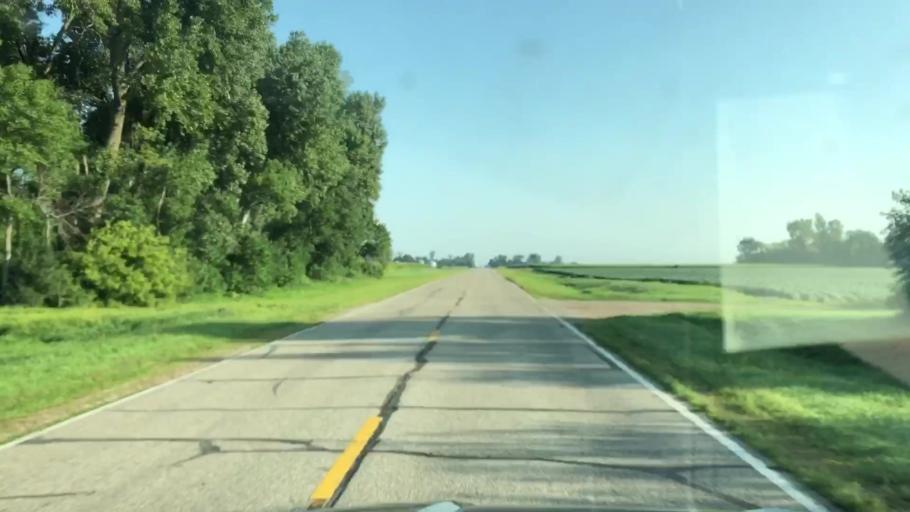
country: US
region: Iowa
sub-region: Lyon County
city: George
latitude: 43.4007
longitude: -95.9982
